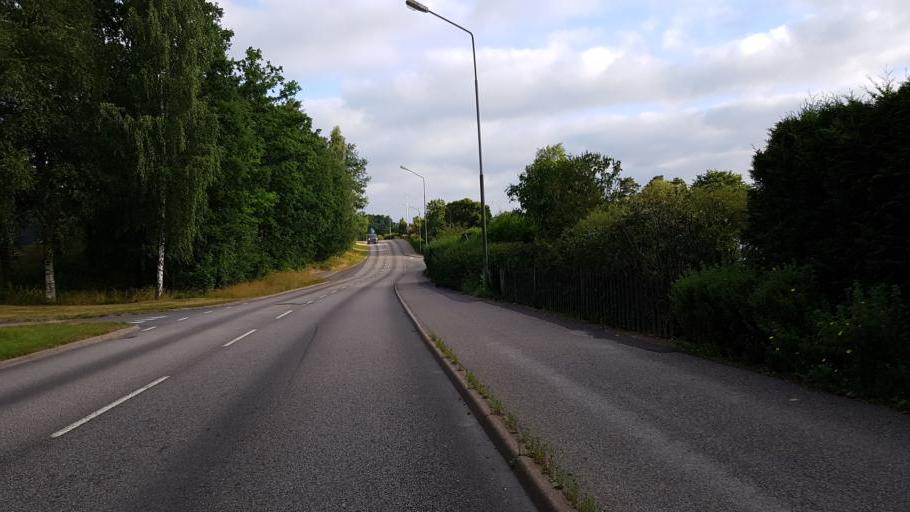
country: SE
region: Vaestra Goetaland
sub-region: Harryda Kommun
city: Molnlycke
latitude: 57.6504
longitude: 12.1111
